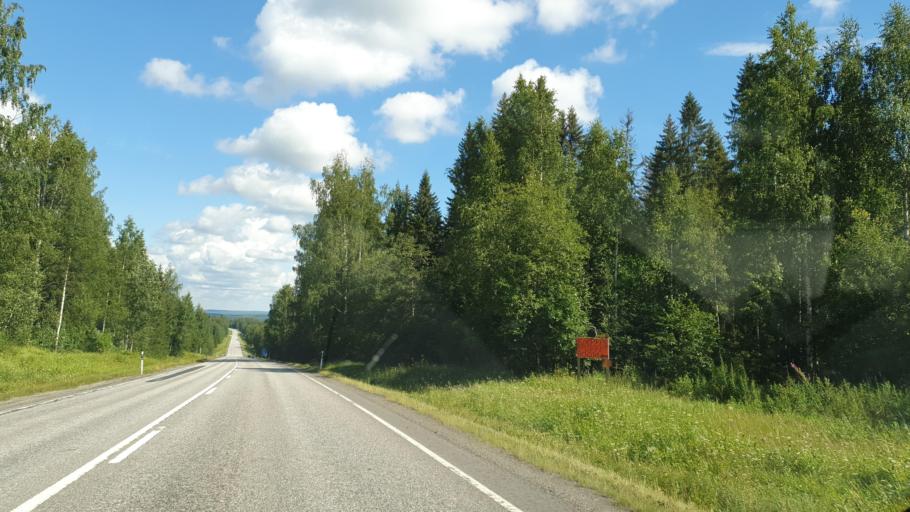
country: FI
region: Northern Savo
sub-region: Ylae-Savo
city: Sonkajaervi
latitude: 63.6856
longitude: 27.3404
